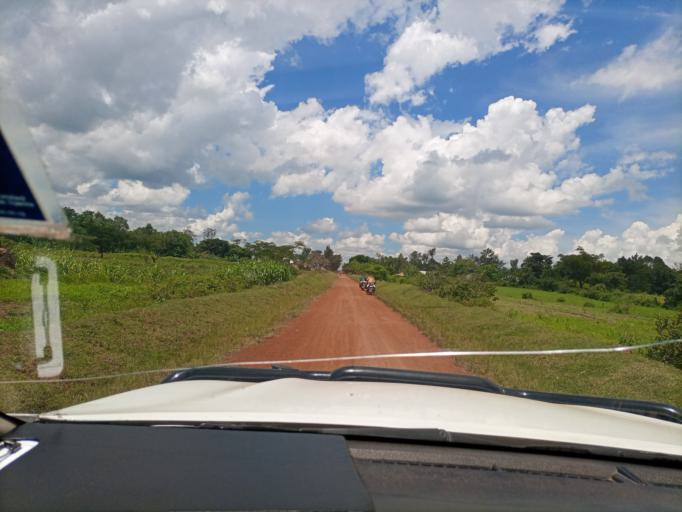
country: UG
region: Eastern Region
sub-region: Busia District
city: Busia
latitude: 0.6334
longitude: 33.9920
